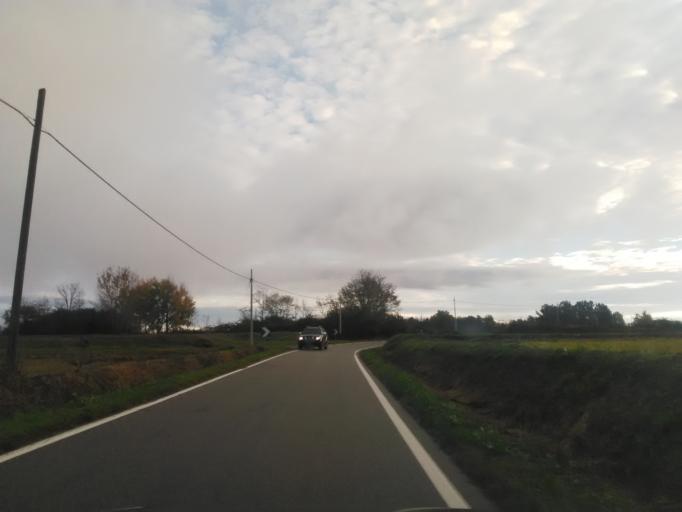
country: IT
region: Piedmont
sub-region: Provincia di Vercelli
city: Lenta
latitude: 45.5552
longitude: 8.3592
